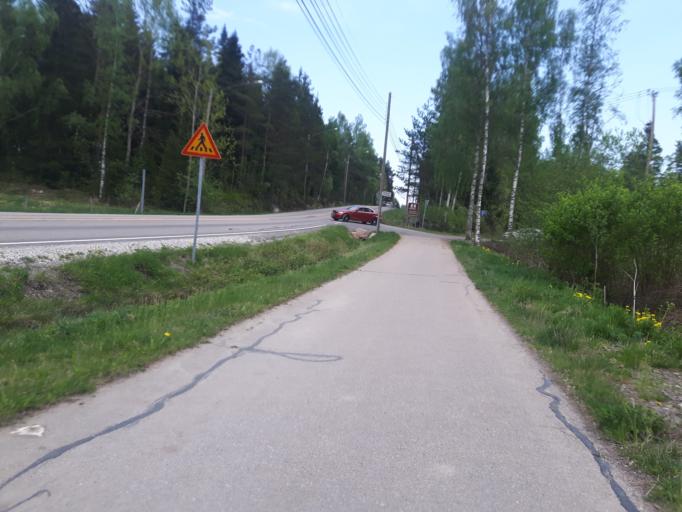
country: FI
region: Uusimaa
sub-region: Porvoo
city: Porvoo
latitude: 60.3915
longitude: 25.7449
